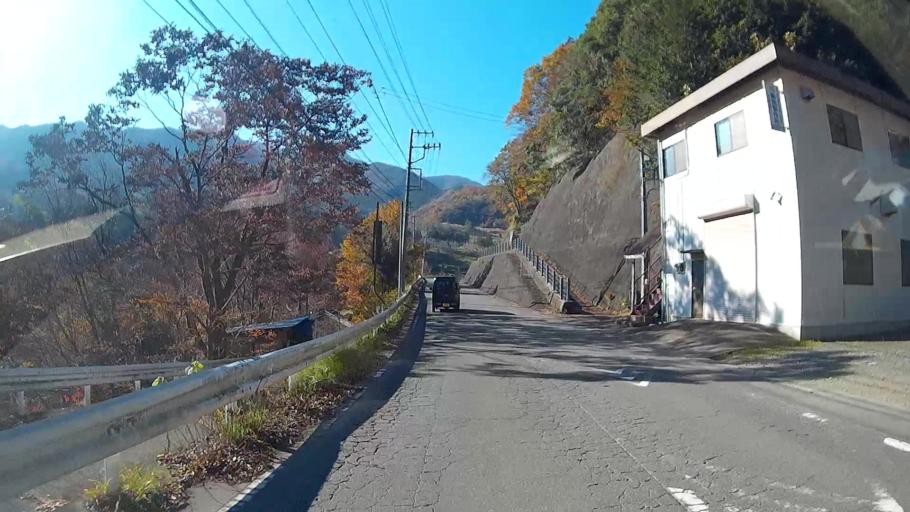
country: JP
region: Yamanashi
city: Uenohara
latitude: 35.5689
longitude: 139.0894
